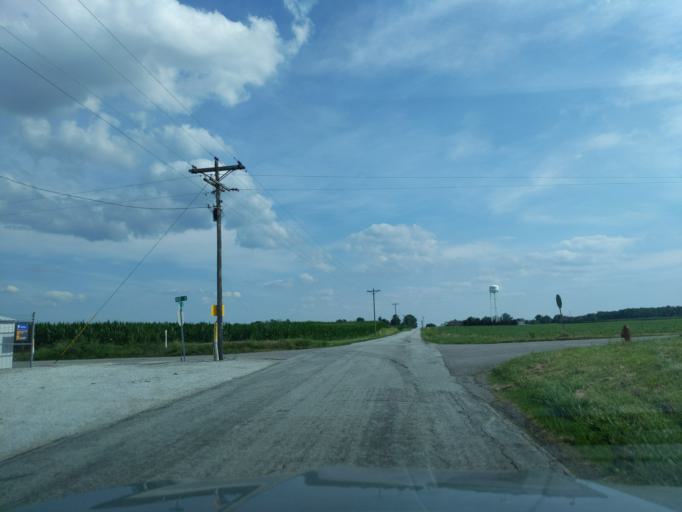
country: US
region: Indiana
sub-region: Decatur County
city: Greensburg
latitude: 39.2784
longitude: -85.4652
